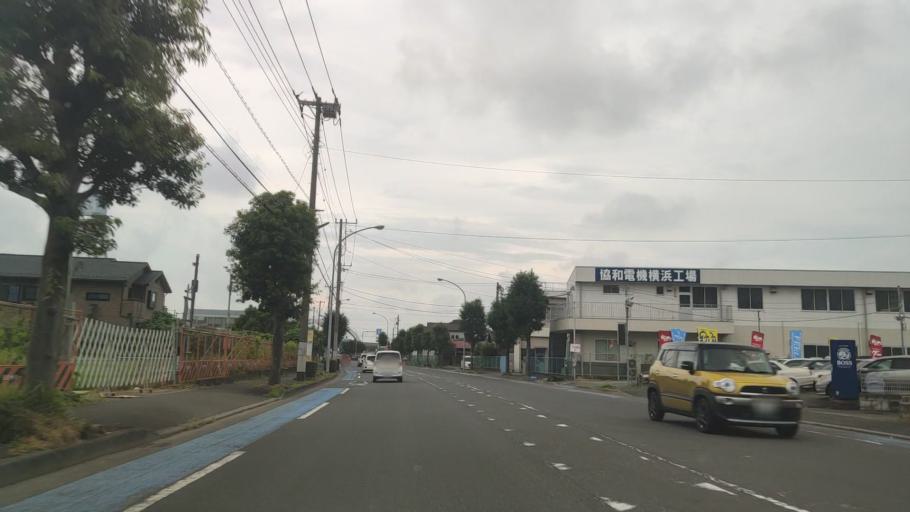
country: JP
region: Kanagawa
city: Fujisawa
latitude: 35.4104
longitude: 139.4842
